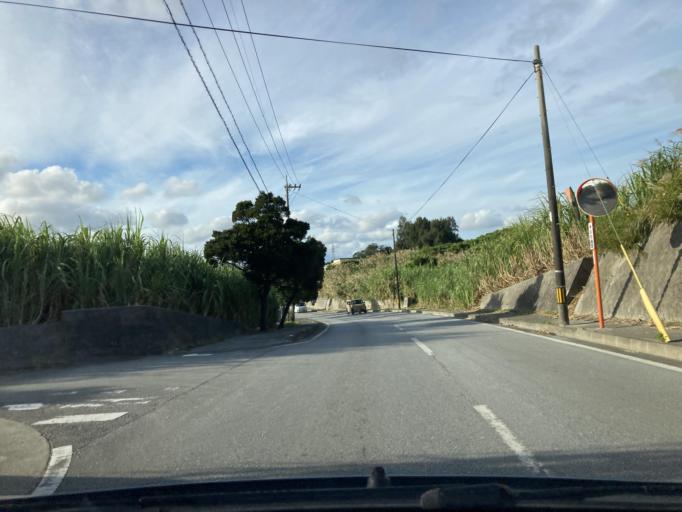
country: JP
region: Okinawa
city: Tomigusuku
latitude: 26.1577
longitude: 127.7385
